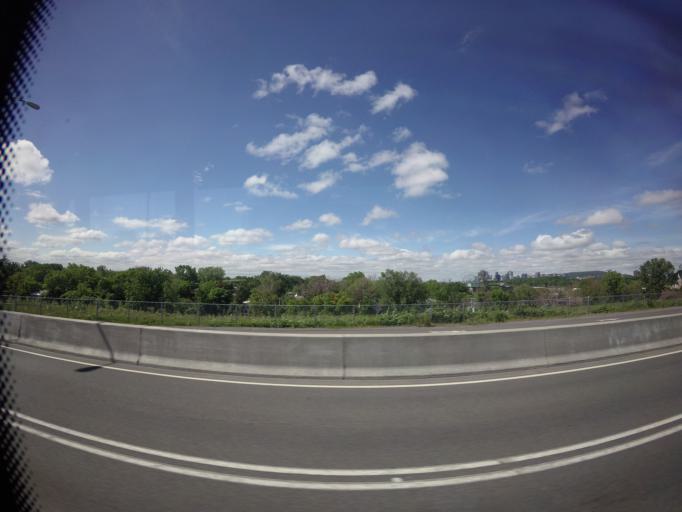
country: CA
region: Quebec
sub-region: Monteregie
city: Longueuil
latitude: 45.5215
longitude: -73.5168
